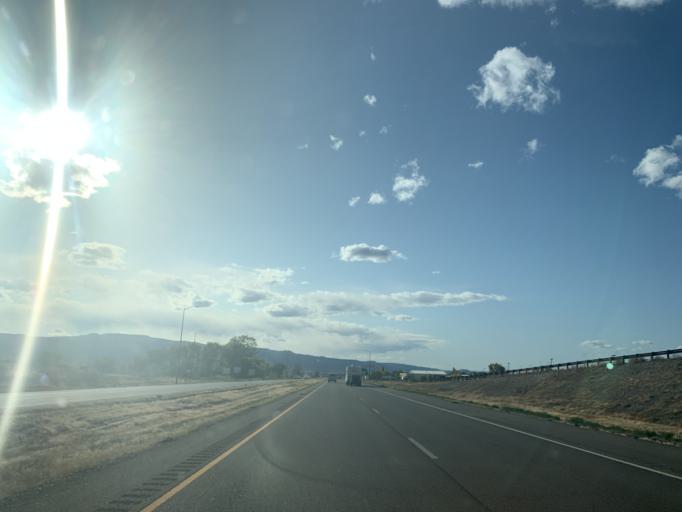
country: US
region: Colorado
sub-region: Mesa County
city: Redlands
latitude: 39.1140
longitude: -108.6090
